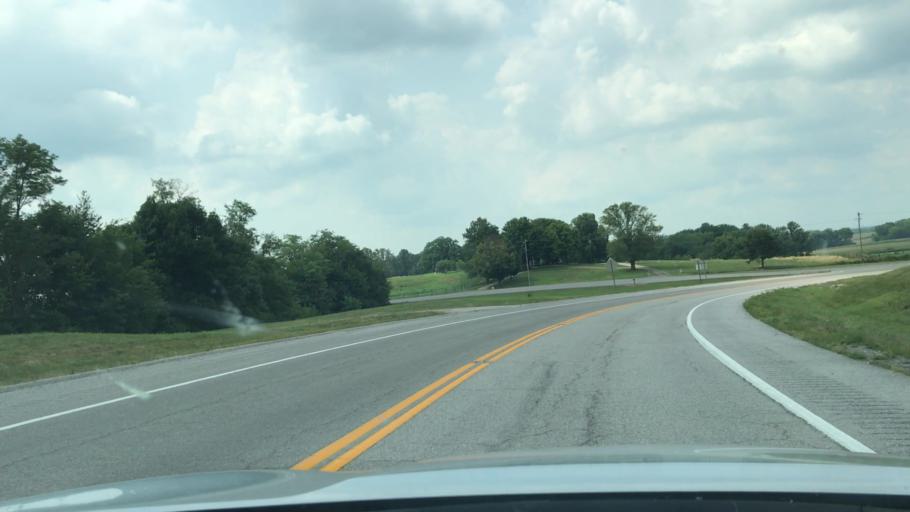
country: US
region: Kentucky
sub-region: Todd County
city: Elkton
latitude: 36.8062
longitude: -87.1208
